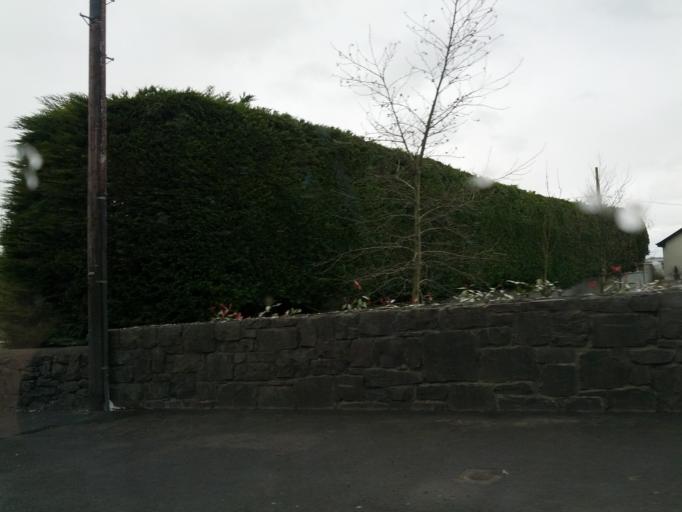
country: IE
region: Connaught
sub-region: County Galway
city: Oranmore
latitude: 53.2512
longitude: -8.8435
